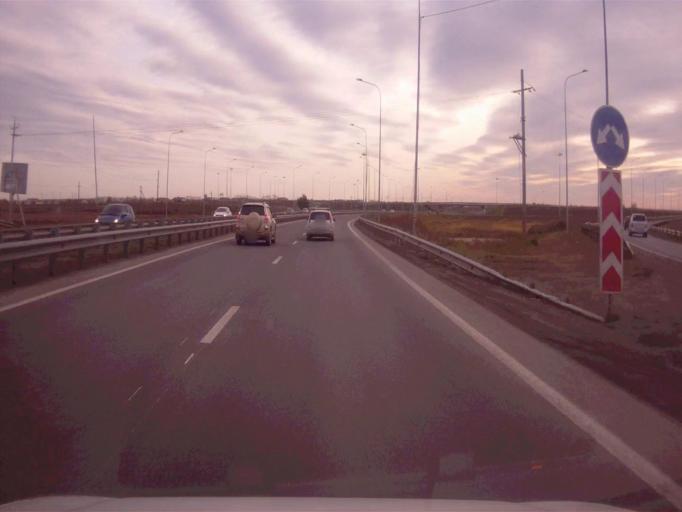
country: RU
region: Chelyabinsk
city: Novosineglazovskiy
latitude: 55.0066
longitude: 61.4532
